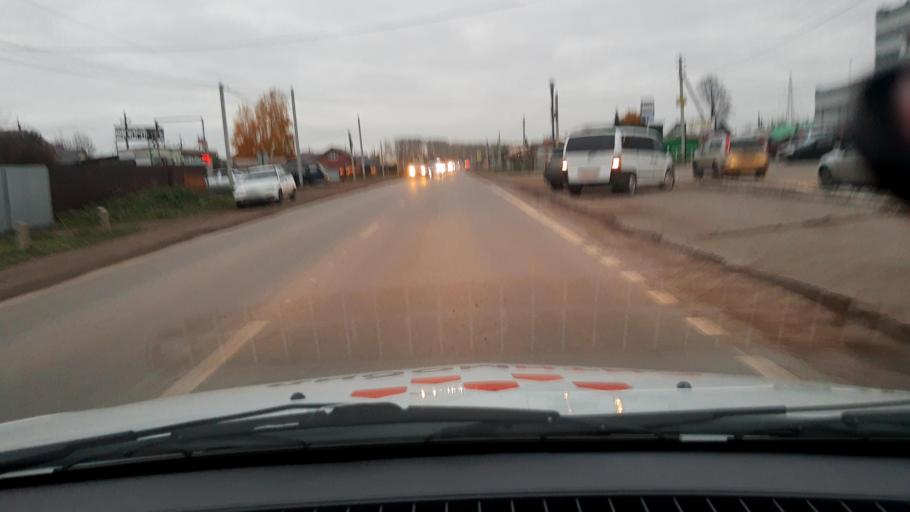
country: RU
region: Bashkortostan
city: Ufa
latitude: 54.6743
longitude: 56.0897
